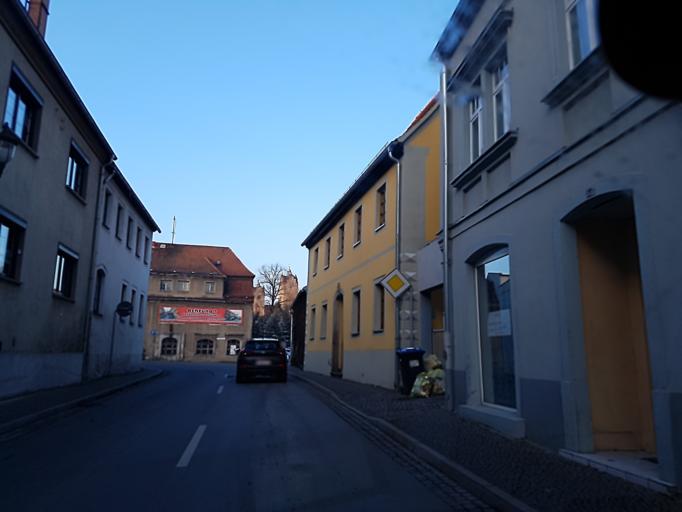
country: DE
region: Saxony
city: Strehla
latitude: 51.3533
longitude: 13.2259
